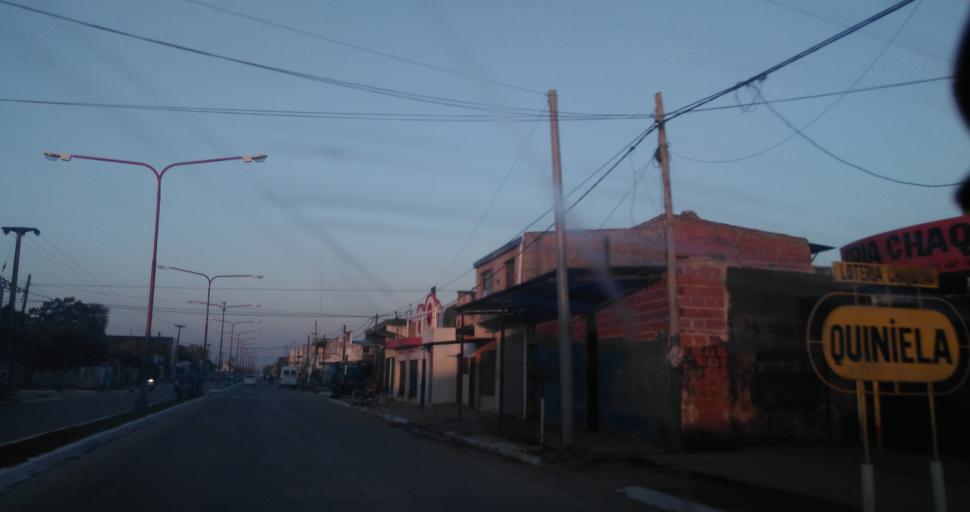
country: AR
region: Chaco
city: Resistencia
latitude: -27.4803
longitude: -58.9762
